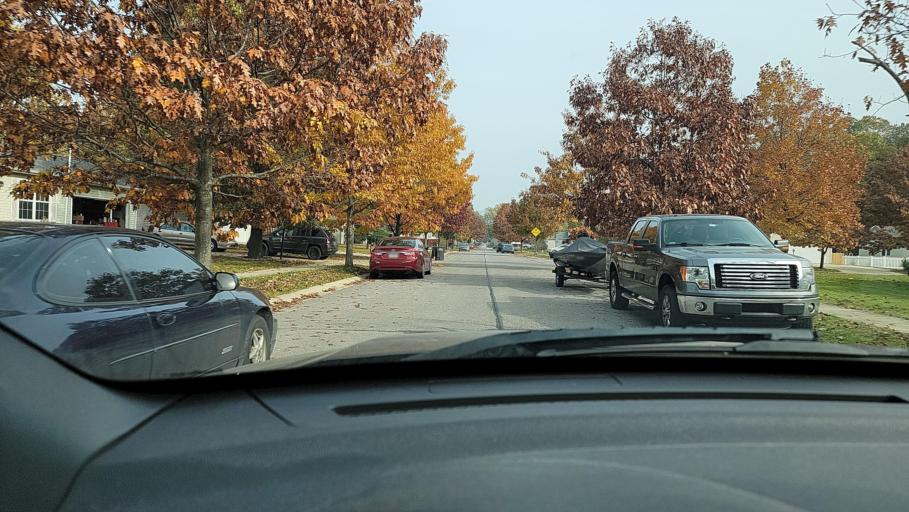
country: US
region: Indiana
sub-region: Porter County
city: Portage
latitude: 41.5907
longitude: -87.1672
